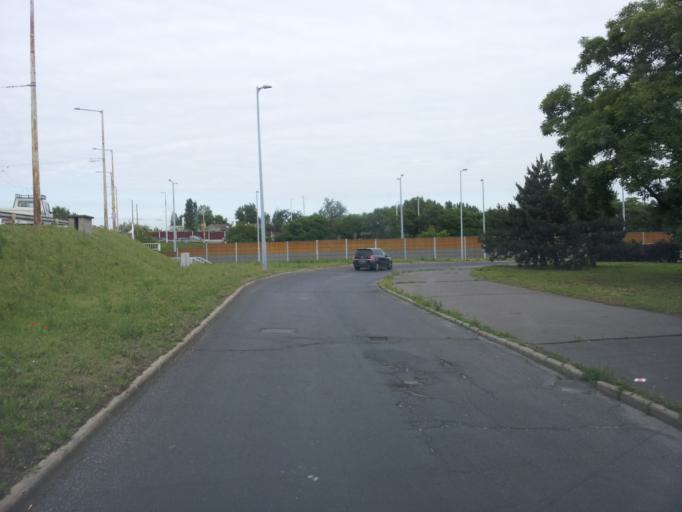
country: HU
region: Budapest
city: Budapest XIV. keruelet
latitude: 47.5241
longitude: 19.0970
